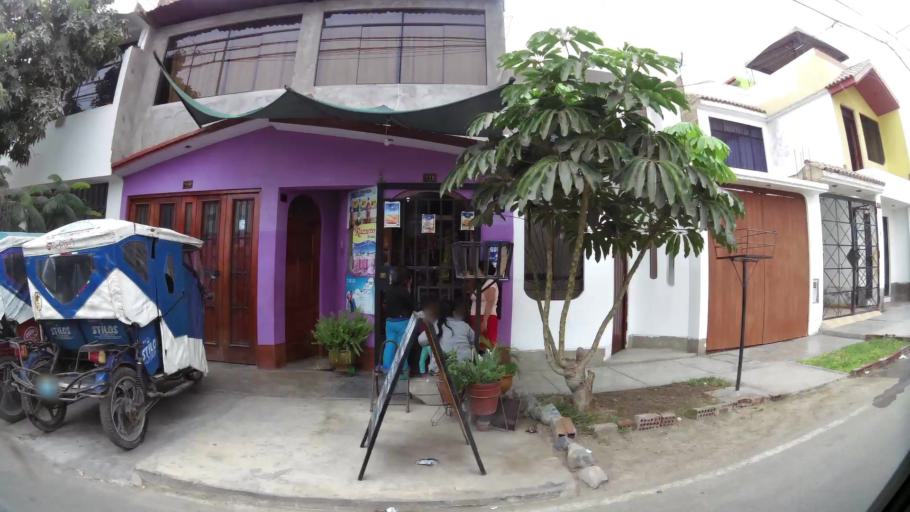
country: PE
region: Lima
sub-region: Lima
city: Santa Rosa
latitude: -11.7881
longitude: -77.1561
